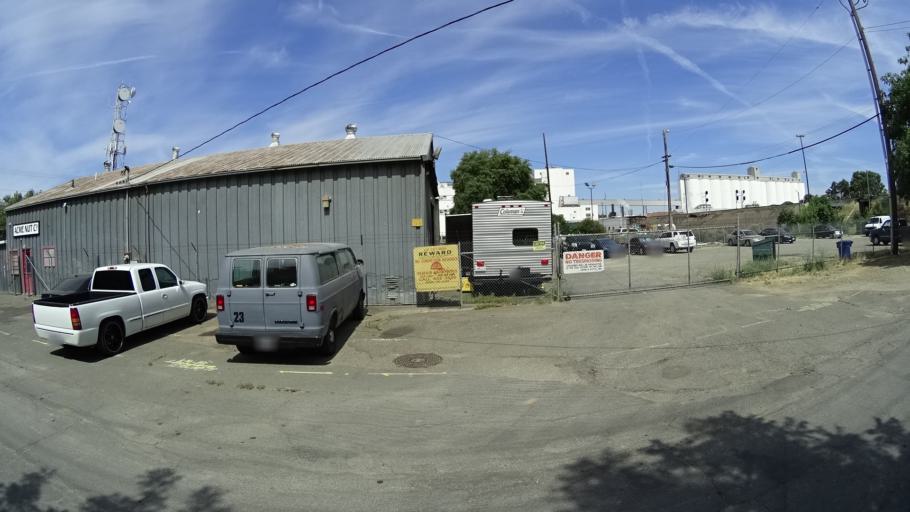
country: US
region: California
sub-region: Sacramento County
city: Sacramento
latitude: 38.5848
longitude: -121.4764
